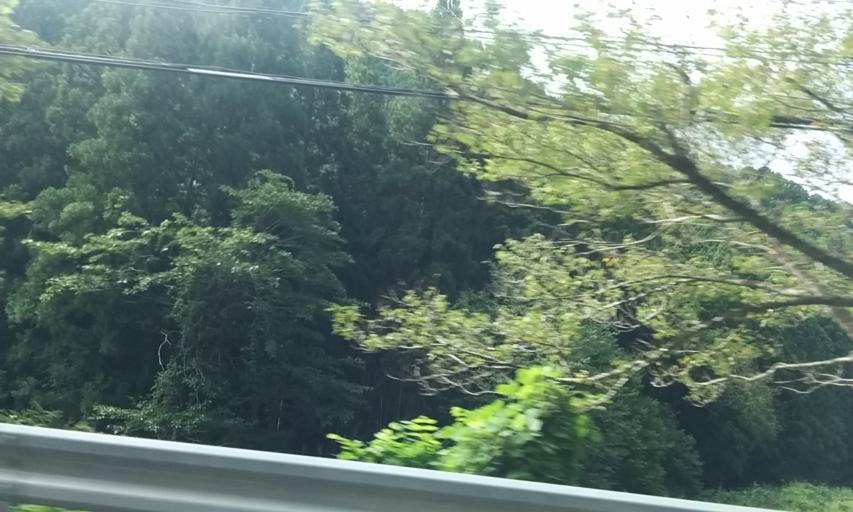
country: JP
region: Gifu
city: Minokamo
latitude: 35.5646
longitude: 137.0870
